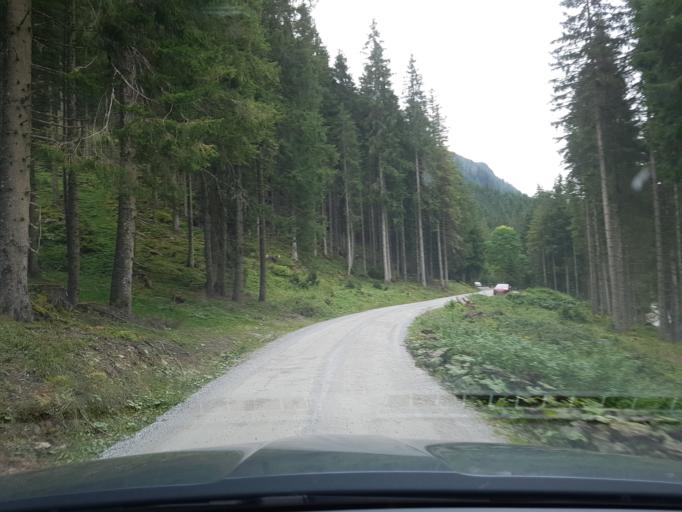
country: AT
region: Salzburg
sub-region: Politischer Bezirk Sankt Johann im Pongau
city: Forstau
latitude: 47.3421
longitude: 13.5765
